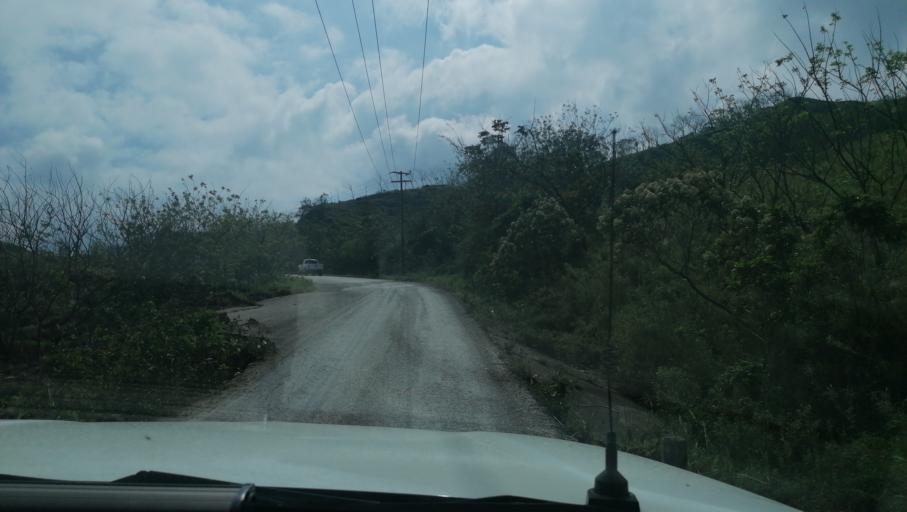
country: MX
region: Chiapas
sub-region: Ocotepec
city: San Pablo Huacano
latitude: 17.2527
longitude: -93.2670
